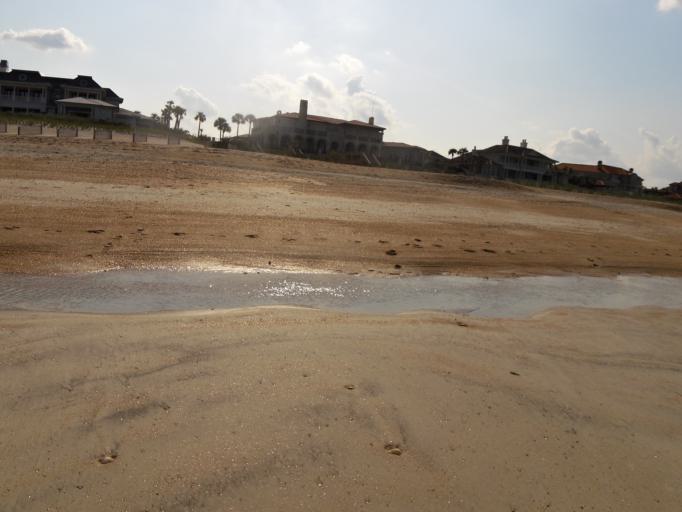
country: US
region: Florida
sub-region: Saint Johns County
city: Palm Valley
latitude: 30.1464
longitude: -81.3515
